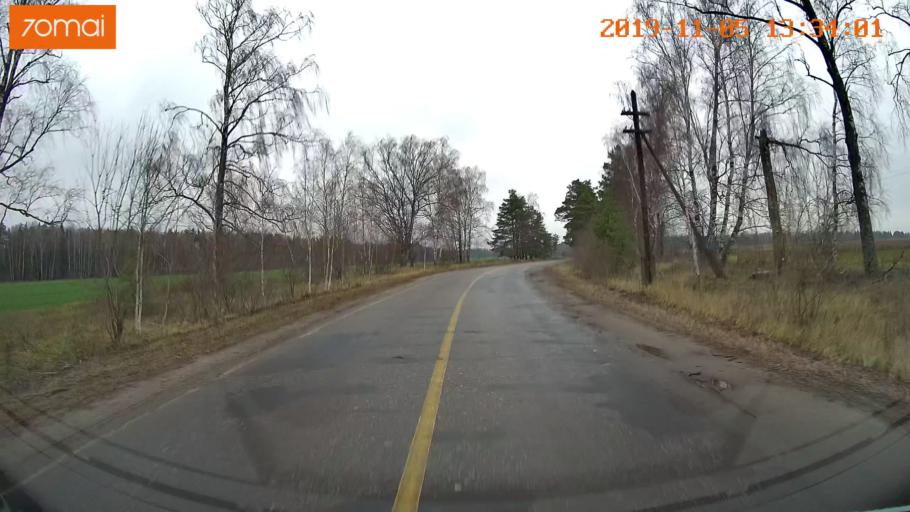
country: RU
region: Ivanovo
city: Shuya
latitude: 56.8971
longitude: 41.3903
